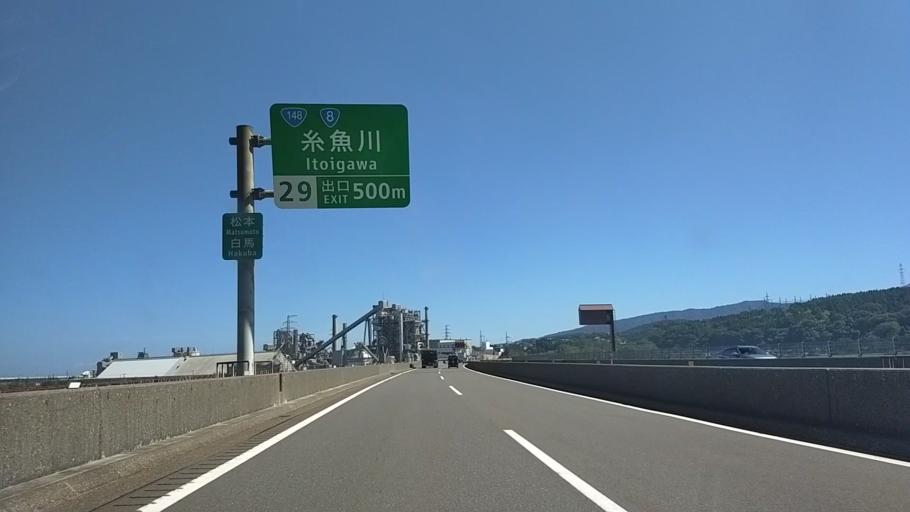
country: JP
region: Niigata
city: Itoigawa
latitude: 37.0243
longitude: 137.8451
